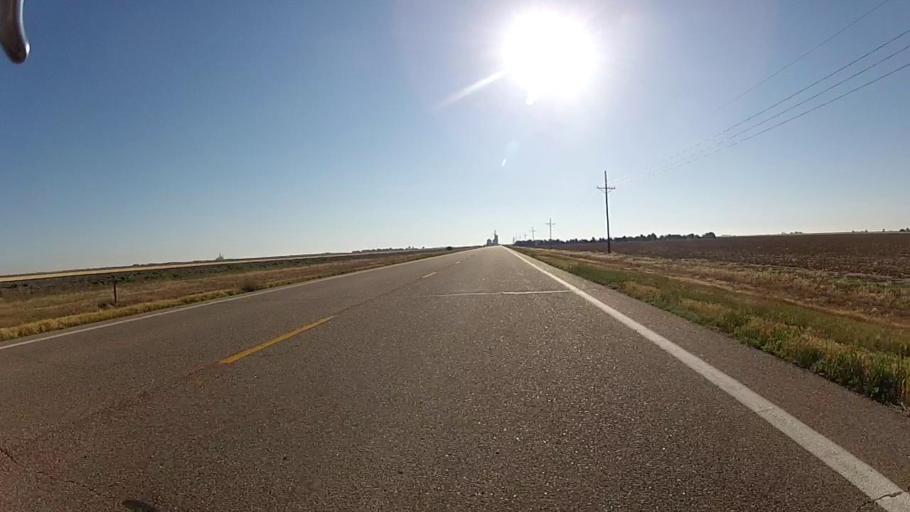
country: US
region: Kansas
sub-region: Haskell County
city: Sublette
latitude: 37.5120
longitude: -100.7413
